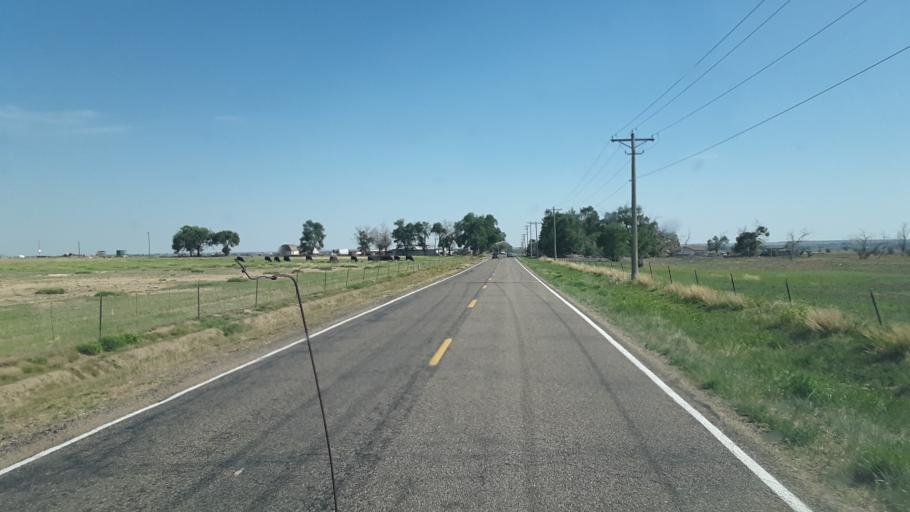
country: US
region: Colorado
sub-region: Crowley County
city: Ordway
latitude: 38.1581
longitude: -103.8569
